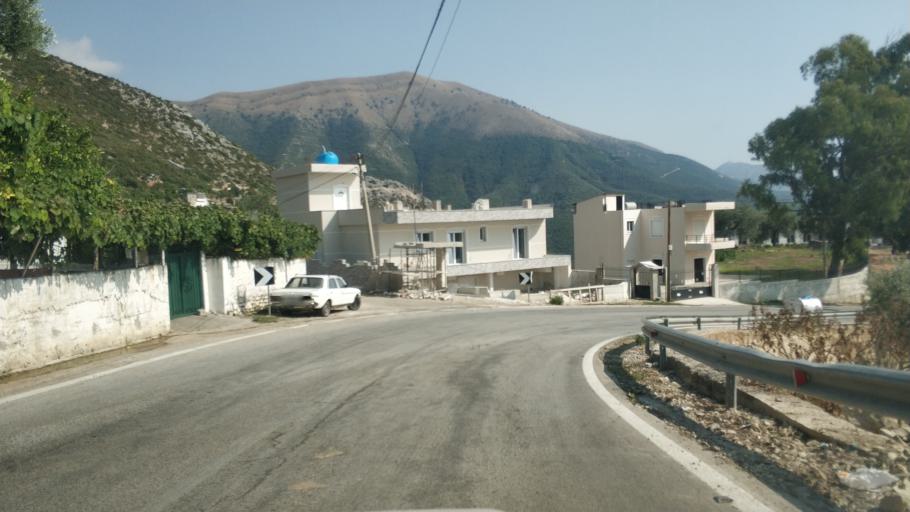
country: AL
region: Vlore
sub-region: Rrethi i Sarandes
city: Lukove
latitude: 40.0157
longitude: 19.8940
